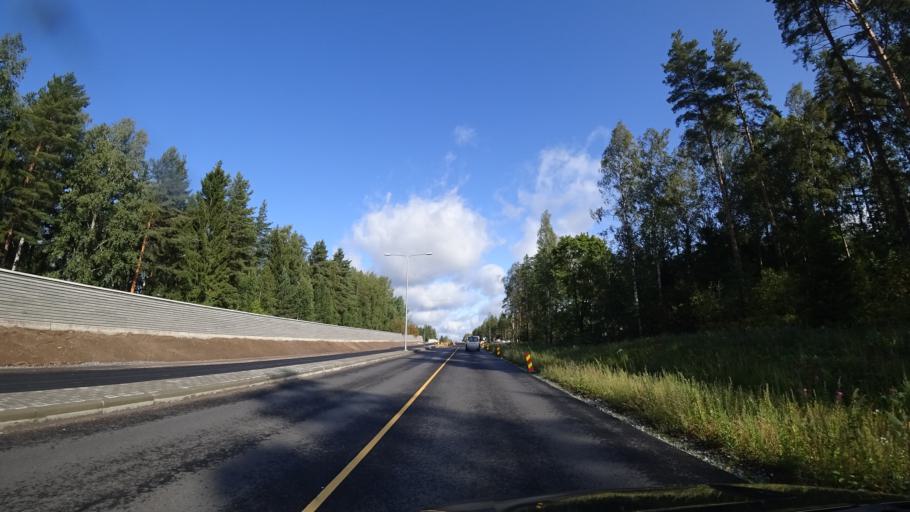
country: FI
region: Uusimaa
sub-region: Helsinki
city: Tuusula
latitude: 60.4091
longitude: 25.0055
